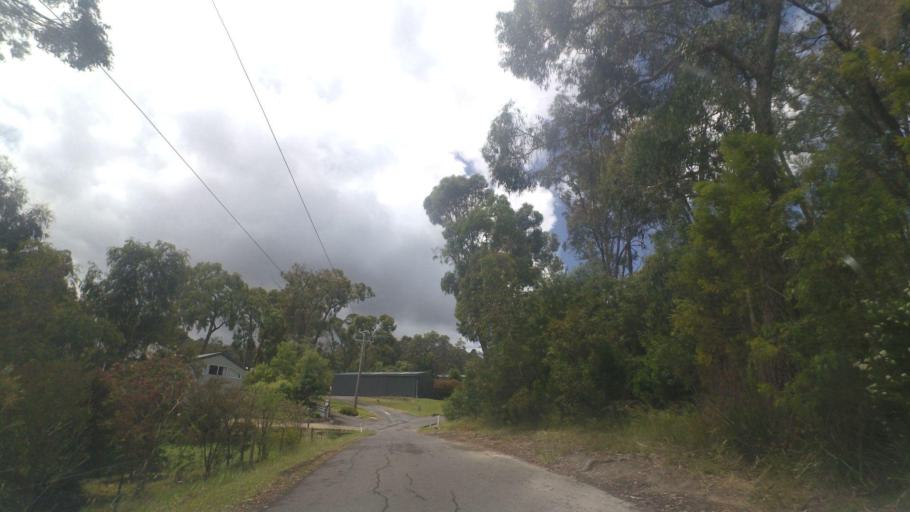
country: AU
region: Victoria
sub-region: Yarra Ranges
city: Mount Evelyn
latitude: -37.7727
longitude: 145.3744
